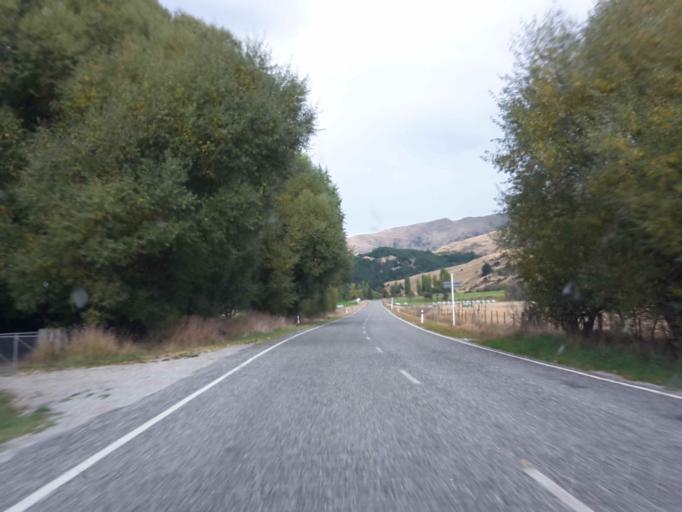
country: NZ
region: Otago
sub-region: Queenstown-Lakes District
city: Wanaka
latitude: -44.7522
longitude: 169.1147
